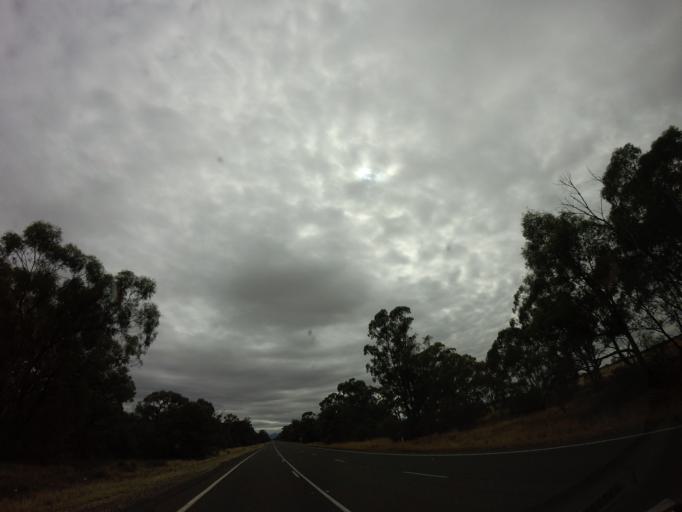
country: AU
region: New South Wales
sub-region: Narrabri
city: Narrabri
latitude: -30.3541
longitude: 149.7475
